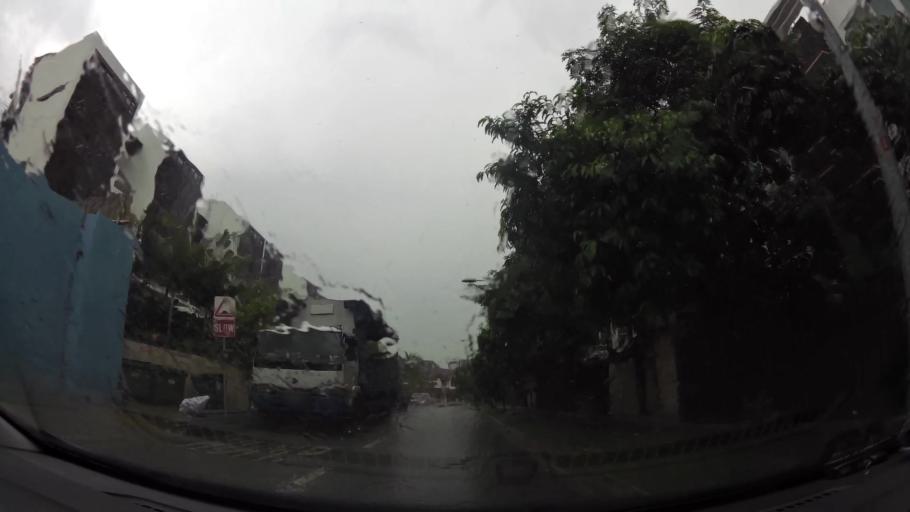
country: MY
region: Johor
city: Kampung Pasir Gudang Baru
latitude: 1.3885
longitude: 103.8555
